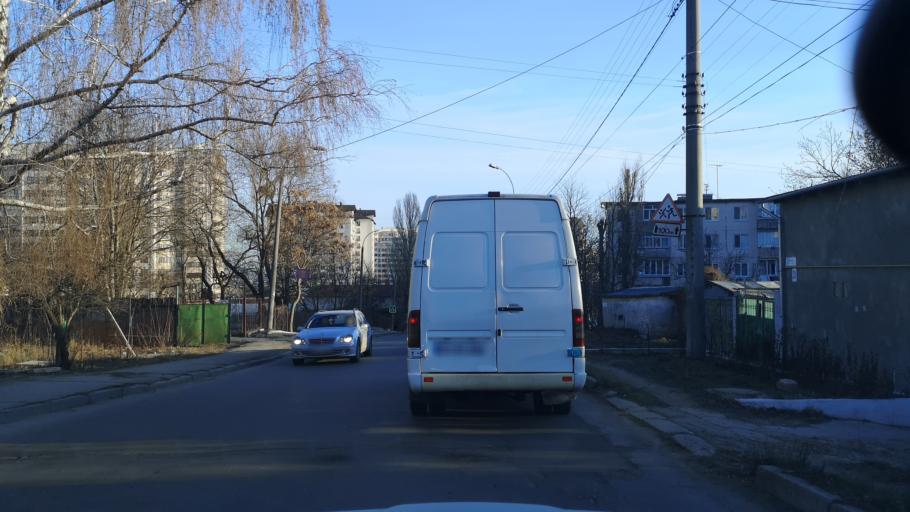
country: MD
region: Chisinau
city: Chisinau
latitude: 46.9849
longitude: 28.8417
